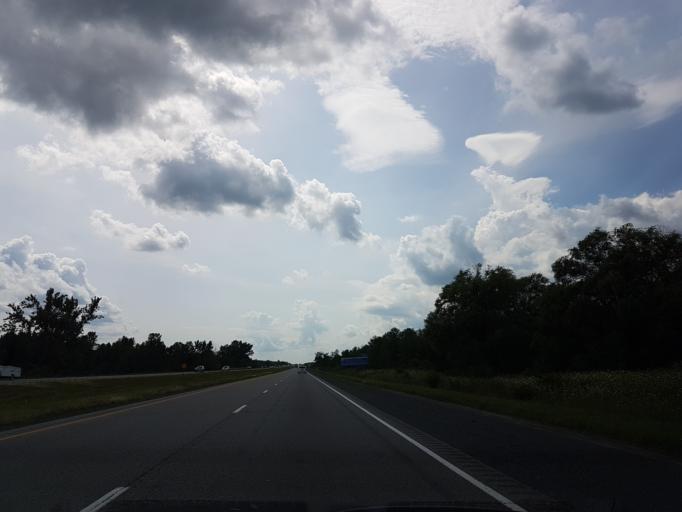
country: US
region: New York
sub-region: St. Lawrence County
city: Norfolk
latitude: 44.9616
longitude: -75.0891
